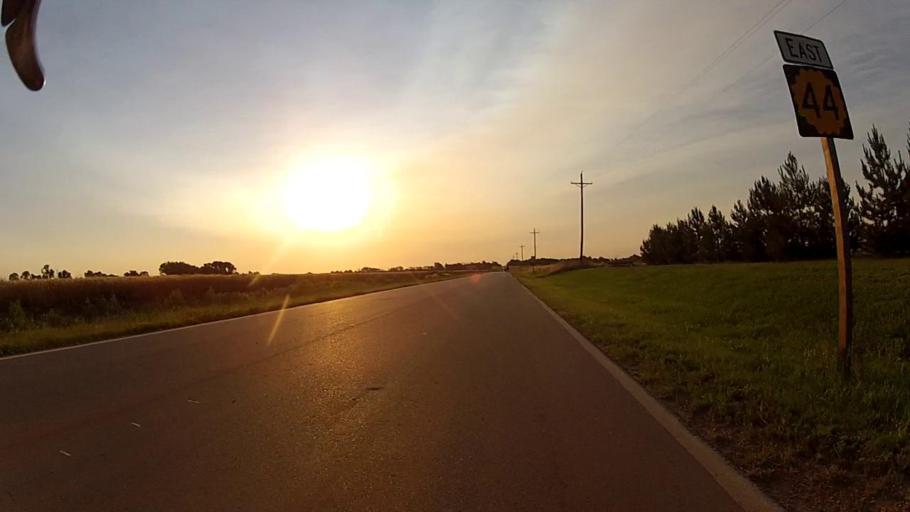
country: US
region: Kansas
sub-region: Harper County
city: Anthony
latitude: 37.1526
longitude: -97.9648
